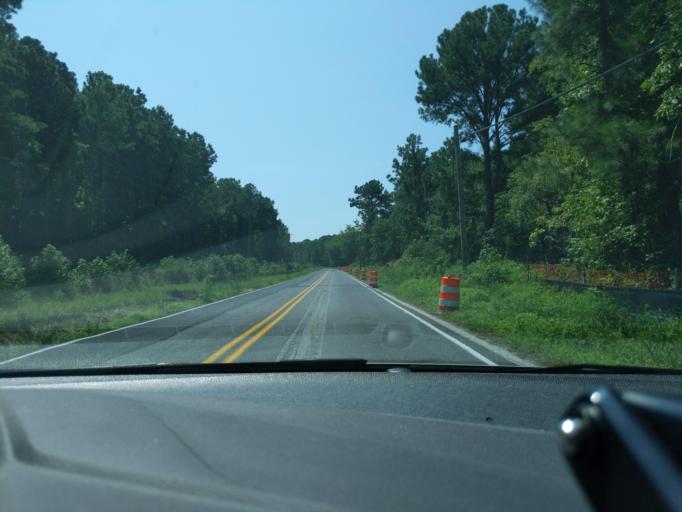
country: US
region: Virginia
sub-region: Northumberland County
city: Heathsville
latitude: 38.0725
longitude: -76.3395
